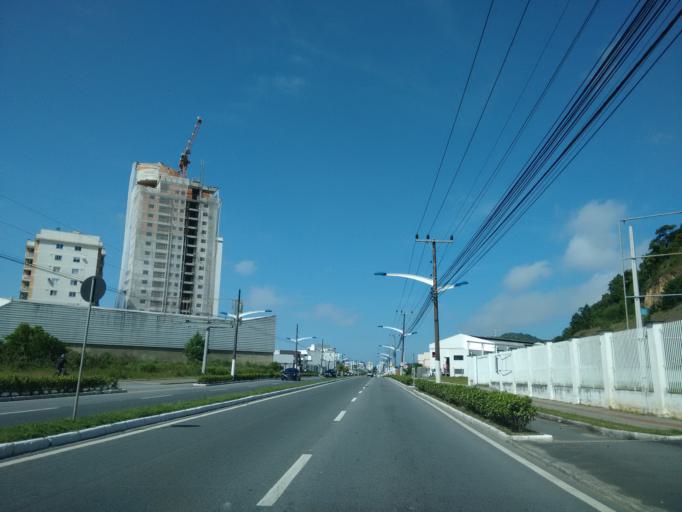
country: BR
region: Santa Catarina
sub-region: Itajai
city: Itajai
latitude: -26.9281
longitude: -48.6827
